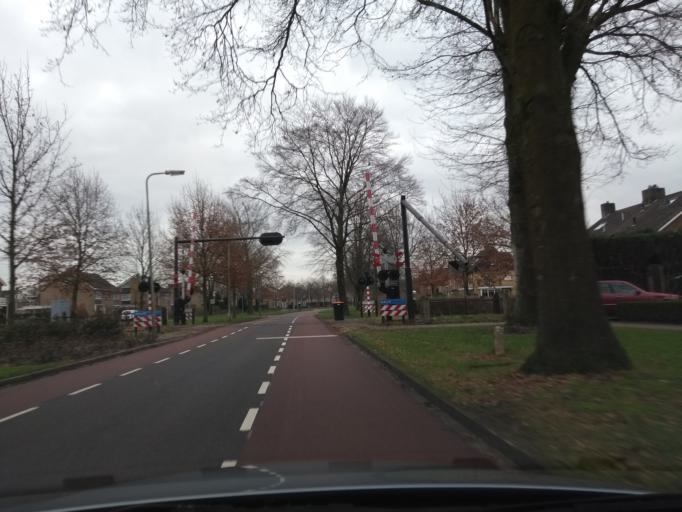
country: NL
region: Overijssel
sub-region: Gemeente Haaksbergen
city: Haaksbergen
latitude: 52.1628
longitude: 6.7475
